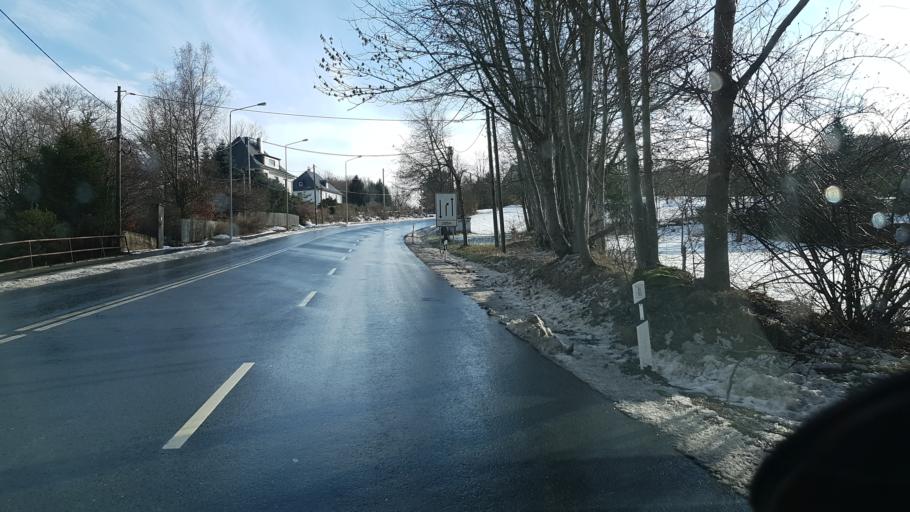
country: DE
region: Saxony
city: Wilkau-Hasslau
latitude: 50.6599
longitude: 12.5552
